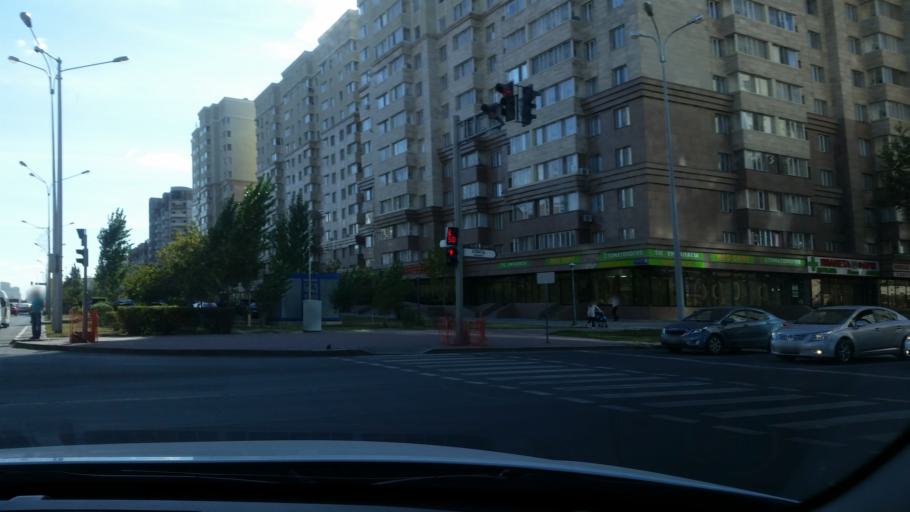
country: KZ
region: Astana Qalasy
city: Astana
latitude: 51.1159
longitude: 71.4347
